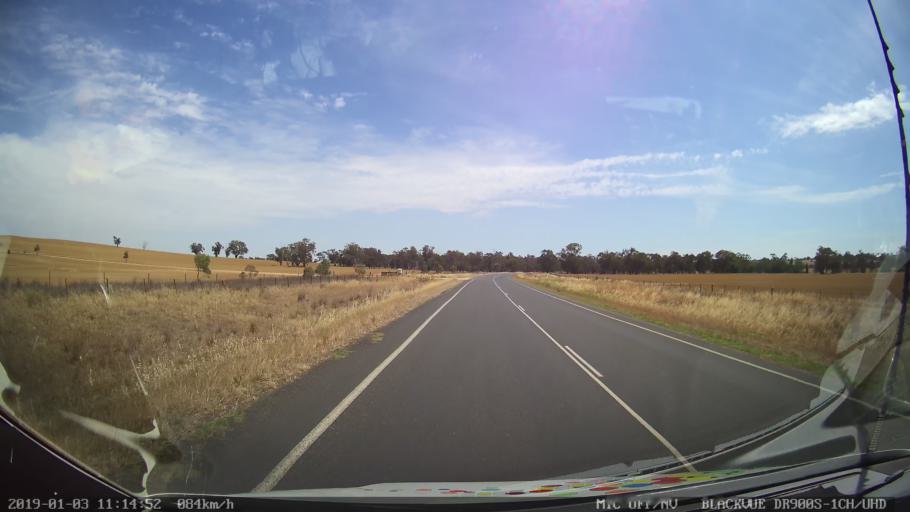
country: AU
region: New South Wales
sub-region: Young
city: Young
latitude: -34.1706
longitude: 148.2615
